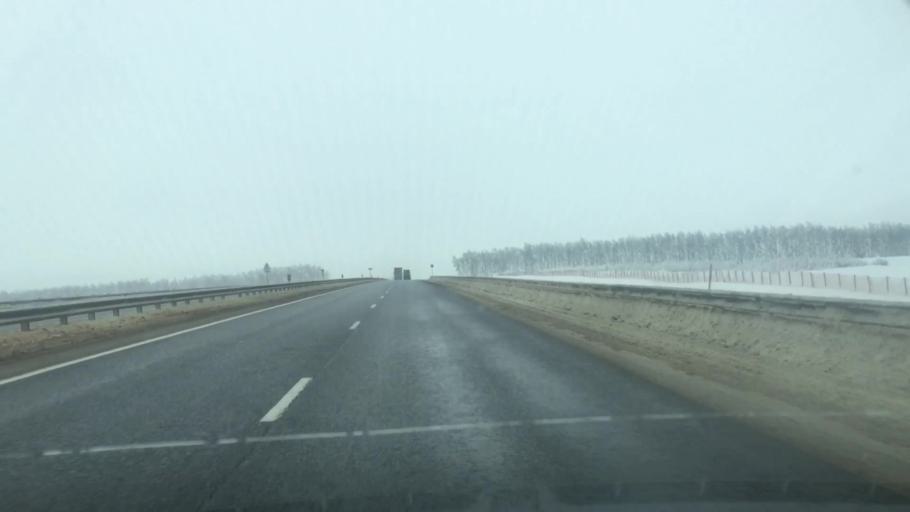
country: RU
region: Lipetsk
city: Stanovoye
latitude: 52.7944
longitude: 38.3346
